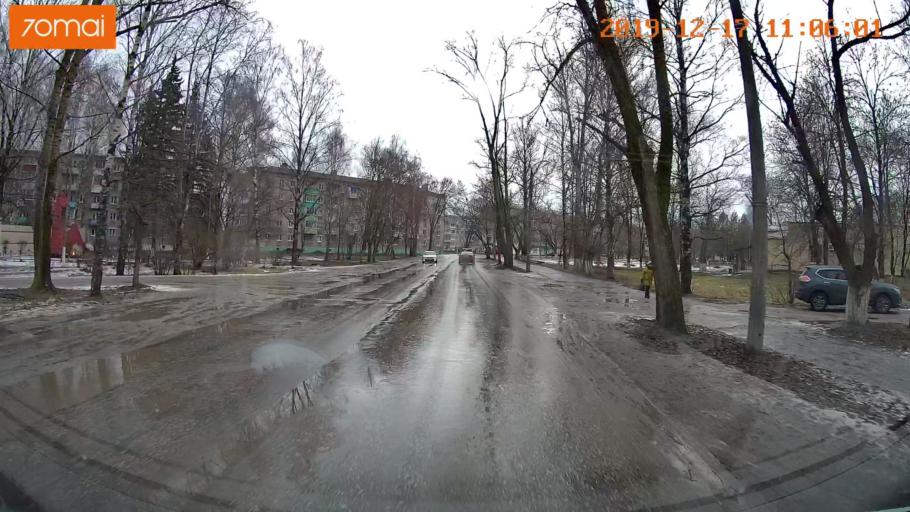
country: RU
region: Vladimir
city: Gus'-Khrustal'nyy
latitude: 55.6175
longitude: 40.6435
